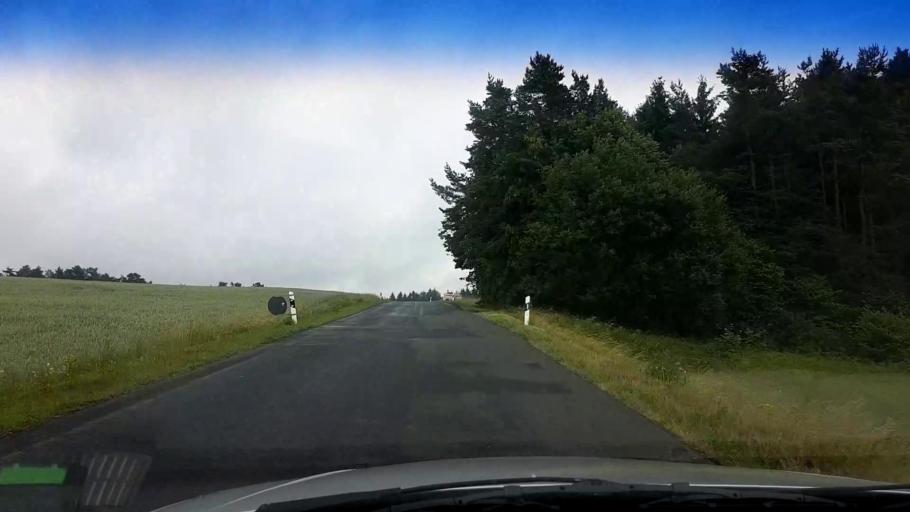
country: DE
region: Bavaria
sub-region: Upper Franconia
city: Wattendorf
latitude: 50.0530
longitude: 11.1238
